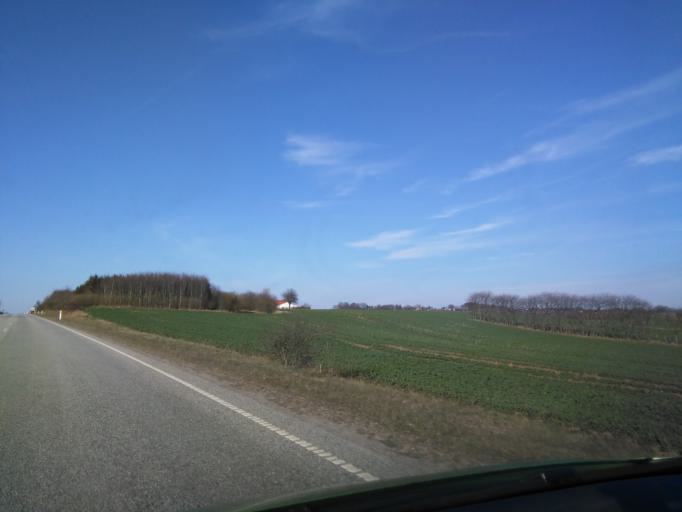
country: DK
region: Central Jutland
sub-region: Horsens Kommune
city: Braedstrup
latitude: 55.9195
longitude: 9.6741
